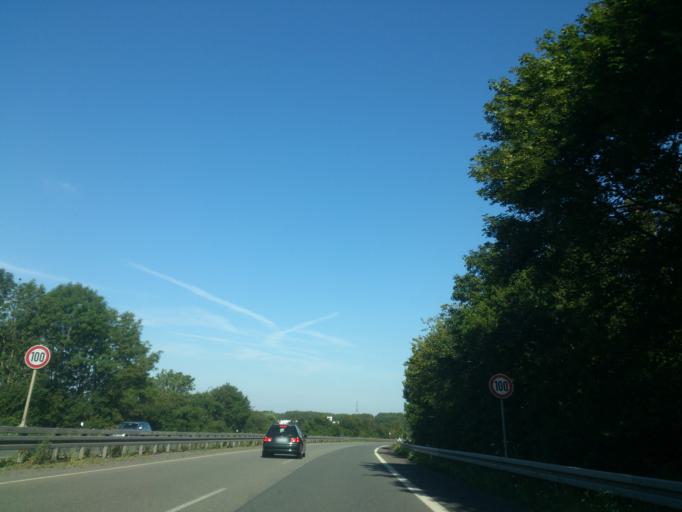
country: DE
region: North Rhine-Westphalia
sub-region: Regierungsbezirk Detmold
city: Paderborn
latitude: 51.7022
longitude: 8.7255
